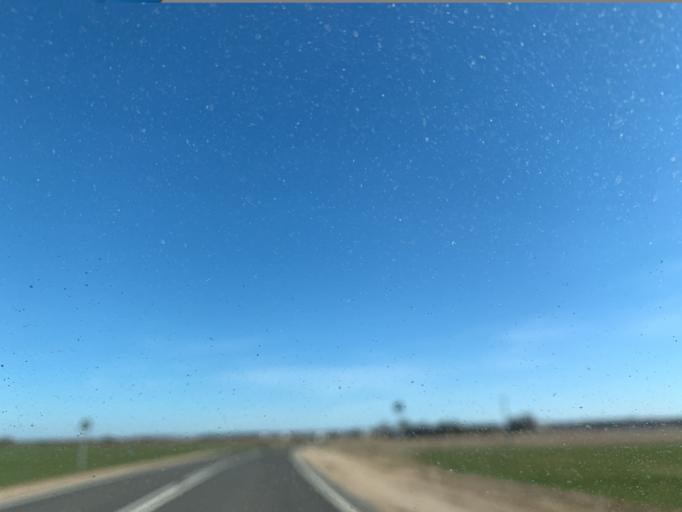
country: BY
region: Minsk
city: Nyasvizh
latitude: 53.2241
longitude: 26.7095
